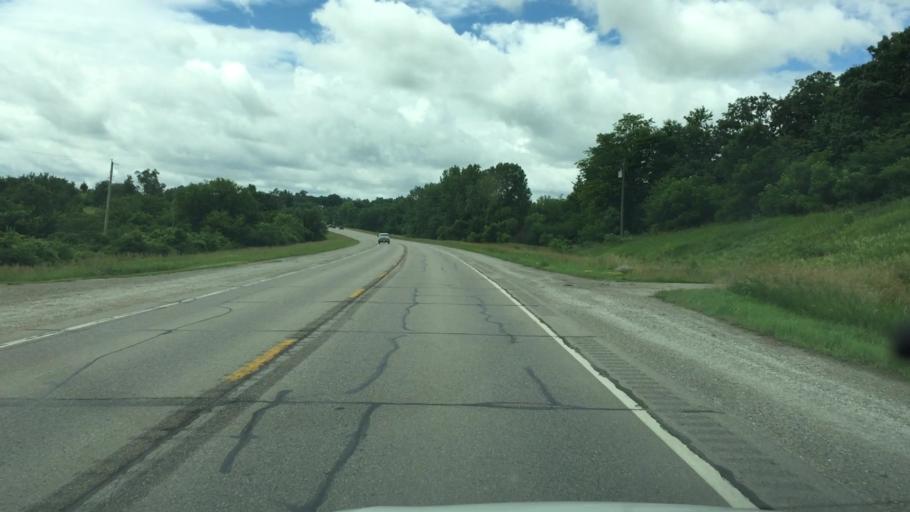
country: US
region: Iowa
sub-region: Jasper County
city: Monroe
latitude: 41.5374
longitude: -93.1008
